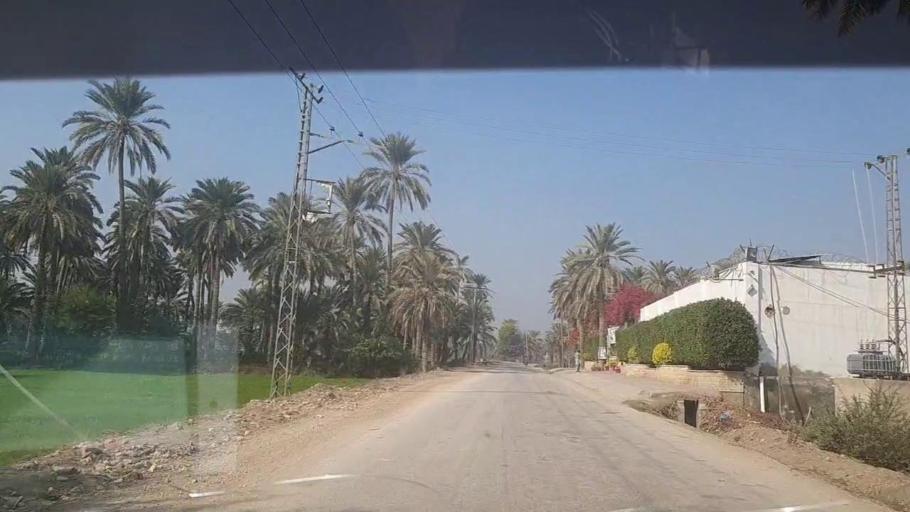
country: PK
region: Sindh
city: Kot Diji
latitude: 27.3800
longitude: 68.6904
